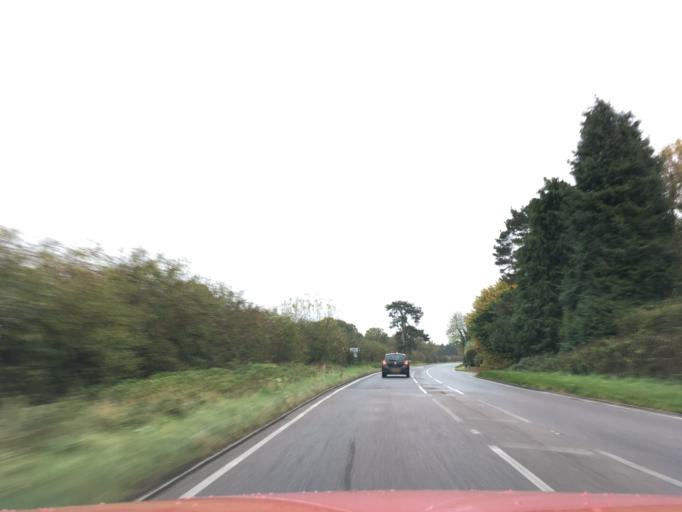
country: GB
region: England
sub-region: West Berkshire
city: Welford
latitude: 51.4267
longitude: -1.4009
